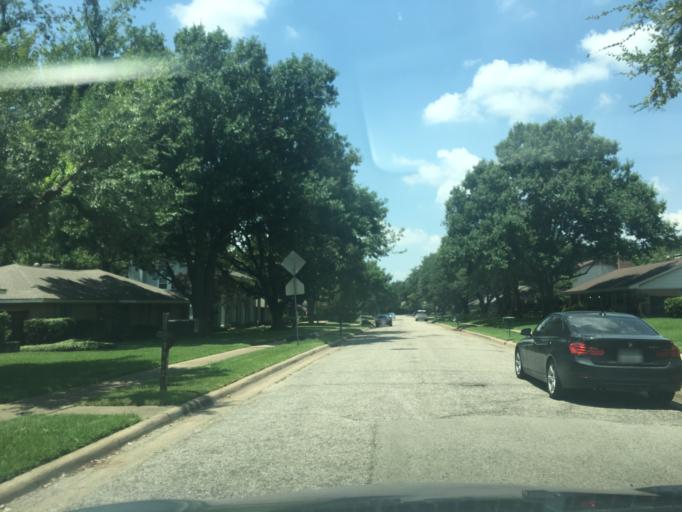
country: US
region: Texas
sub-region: Dallas County
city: Addison
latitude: 32.9196
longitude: -96.8445
